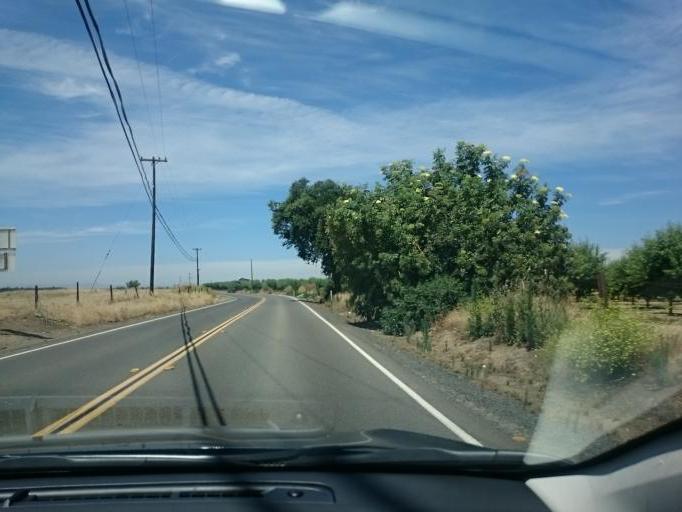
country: US
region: California
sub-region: Stanislaus County
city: Waterford
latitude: 37.6465
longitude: -120.6840
